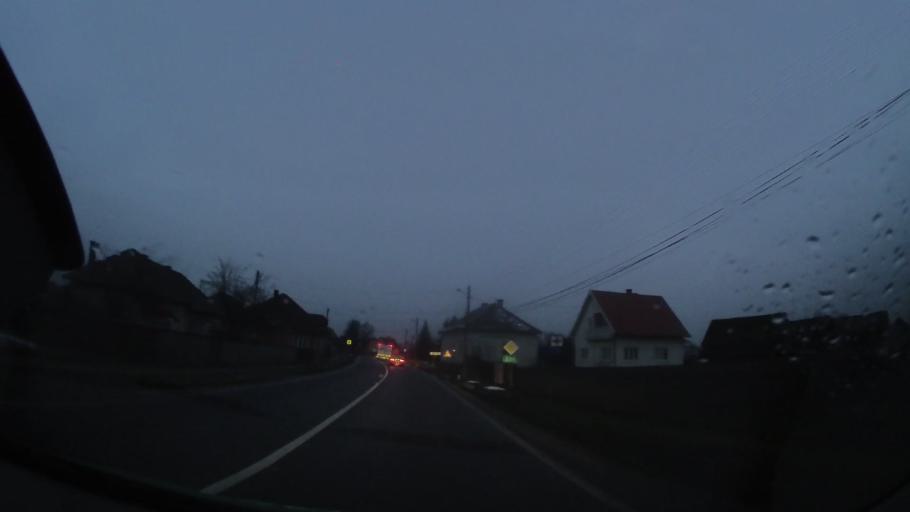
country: RO
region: Harghita
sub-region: Comuna Ditrau
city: Ditrau
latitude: 46.8050
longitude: 25.4948
